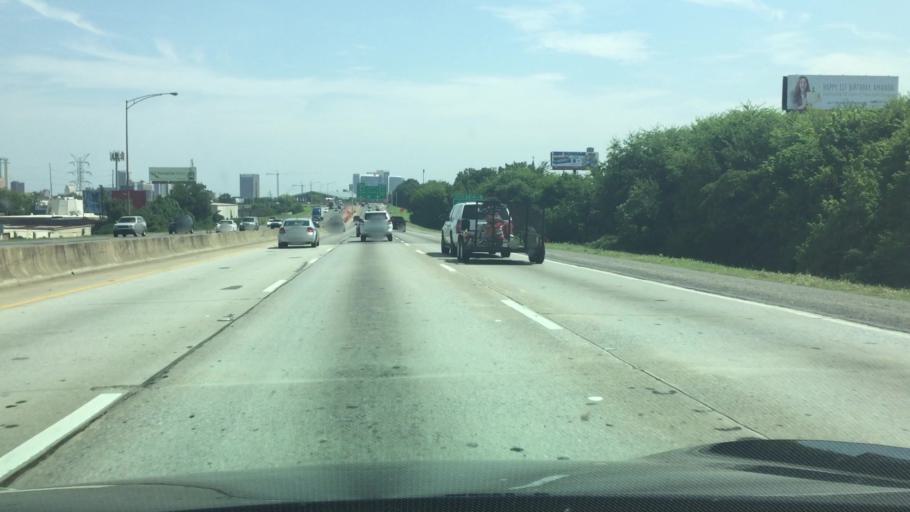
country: US
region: Alabama
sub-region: Jefferson County
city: Homewood
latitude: 33.4926
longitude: -86.8200
